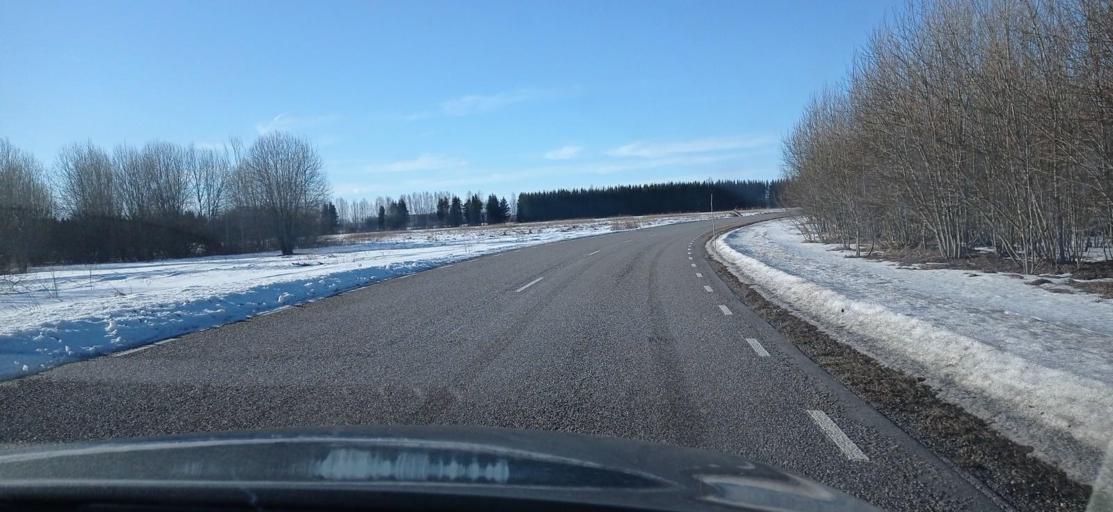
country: EE
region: Tartu
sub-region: Alatskivi vald
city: Kallaste
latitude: 58.4922
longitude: 27.2319
